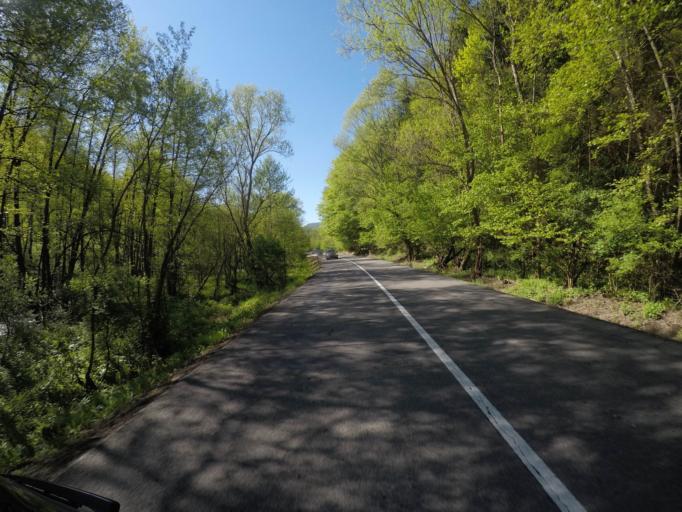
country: SK
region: Banskobystricky
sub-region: Okres Banska Bystrica
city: Banska Stiavnica
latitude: 48.5260
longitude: 19.0041
